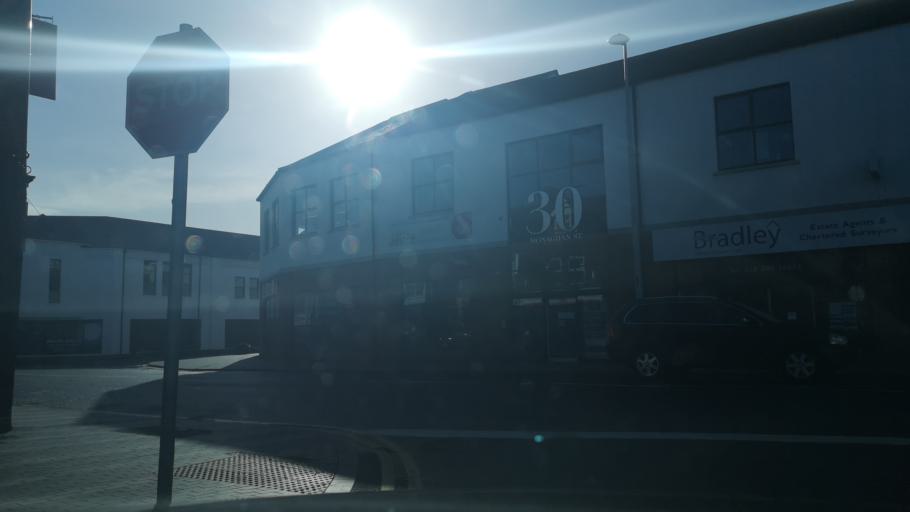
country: GB
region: Northern Ireland
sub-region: Newry and Mourne District
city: Newry
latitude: 54.1773
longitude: -6.3439
